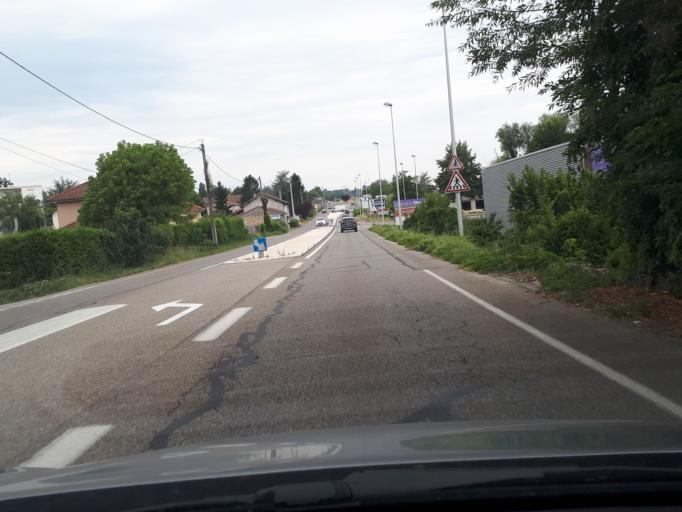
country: FR
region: Rhone-Alpes
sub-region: Departement de l'Isere
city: Domarin
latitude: 45.5868
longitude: 5.2539
